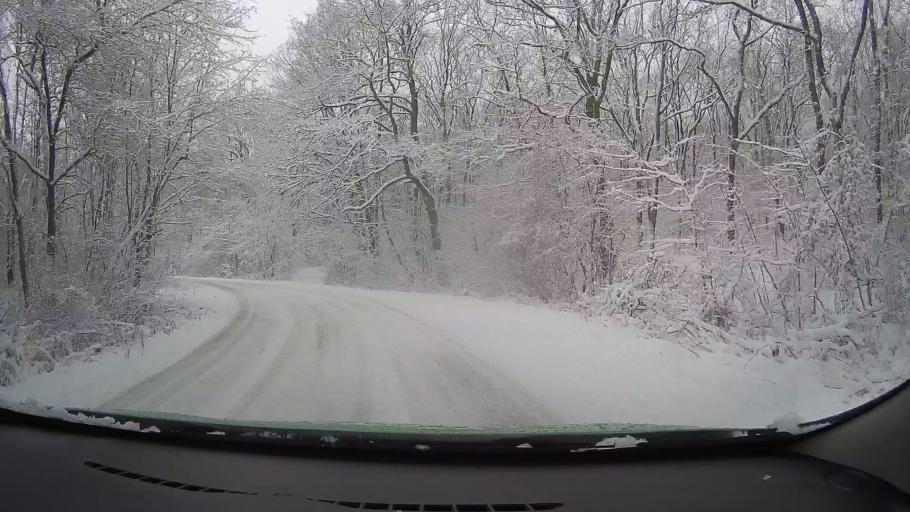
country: RO
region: Hunedoara
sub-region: Municipiul Deva
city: Deva
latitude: 45.8549
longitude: 22.8794
